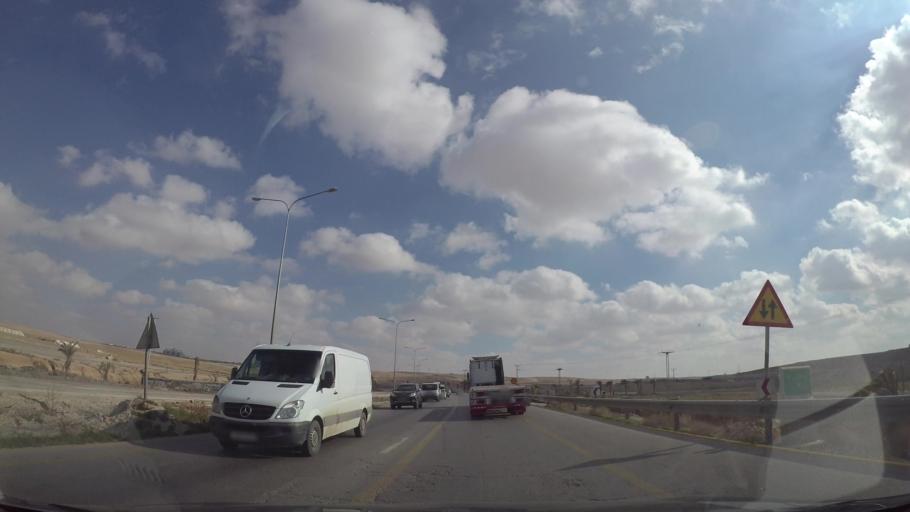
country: JO
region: Amman
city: Al Jizah
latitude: 31.6322
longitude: 35.9850
